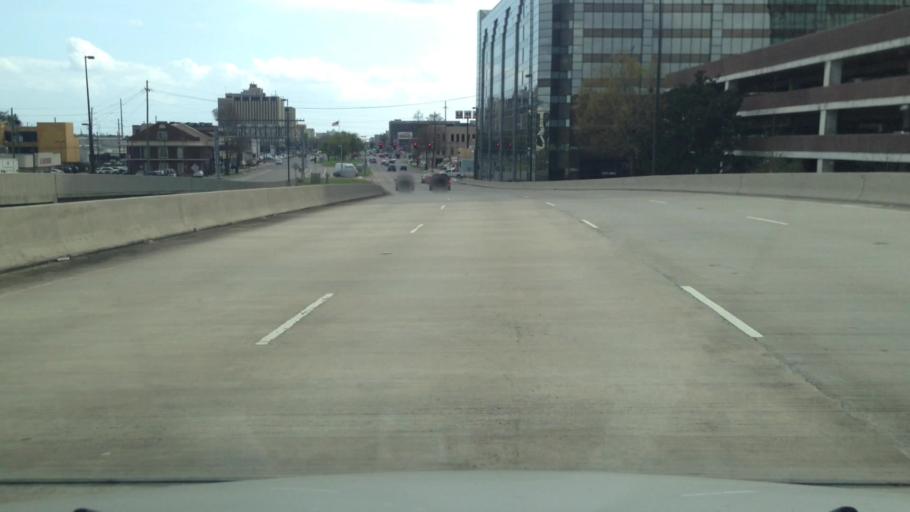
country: US
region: Louisiana
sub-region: Jefferson Parish
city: Metairie
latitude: 30.0197
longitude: -90.1546
